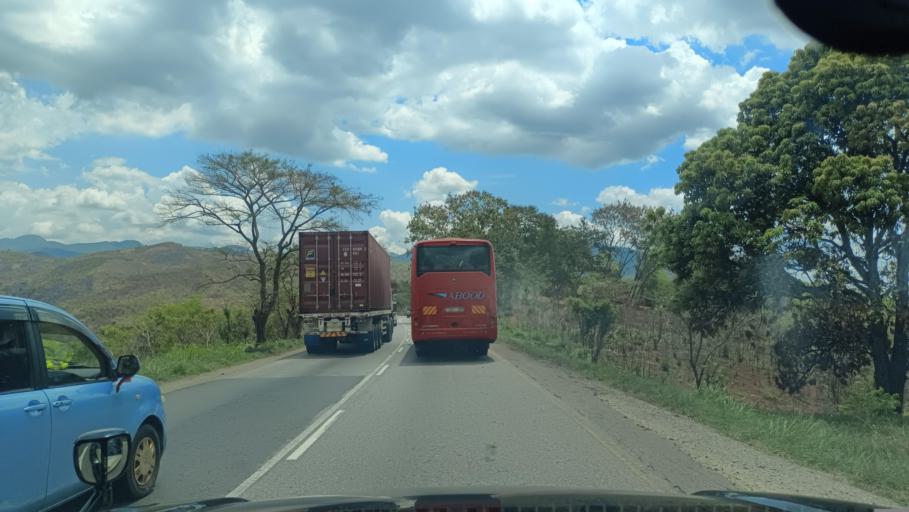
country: TZ
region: Morogoro
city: Mikumi
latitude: -7.4635
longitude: 36.9188
